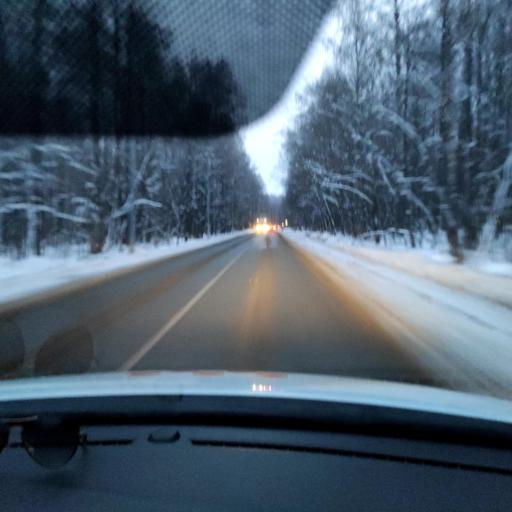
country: RU
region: Tatarstan
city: Vysokaya Gora
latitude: 55.9334
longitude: 49.1691
